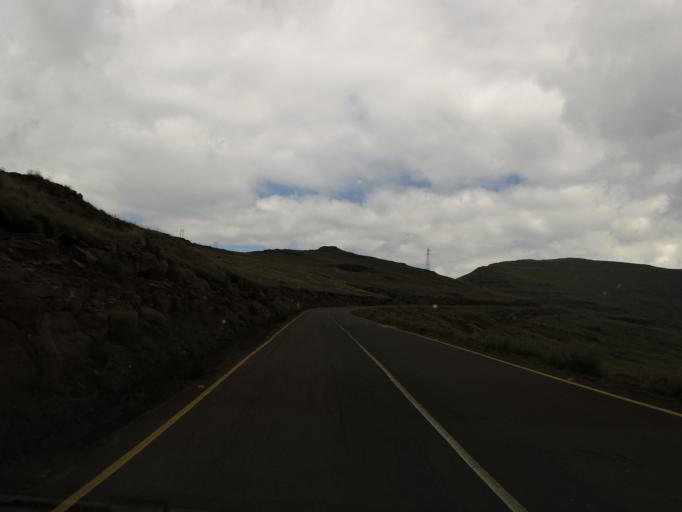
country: LS
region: Butha-Buthe
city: Butha-Buthe
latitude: -29.0974
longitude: 28.4233
